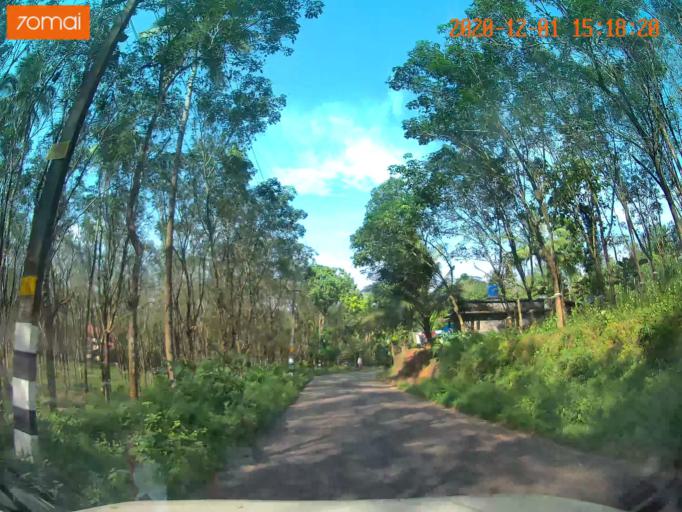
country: IN
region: Kerala
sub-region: Ernakulam
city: Ramamangalam
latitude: 9.9358
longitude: 76.5304
